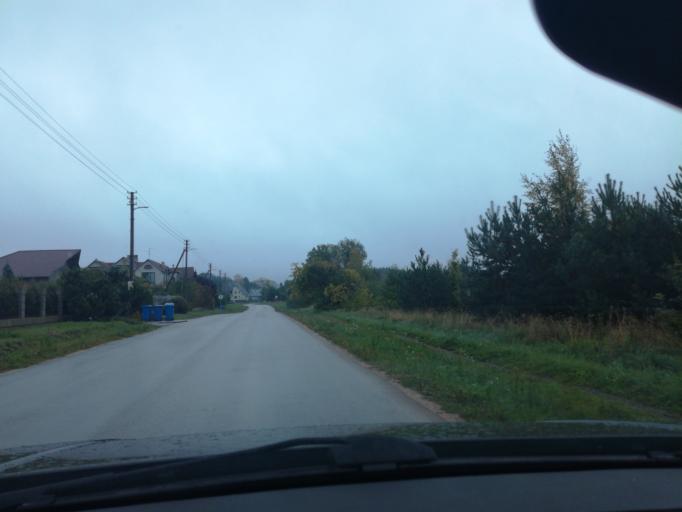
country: LT
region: Alytaus apskritis
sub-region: Alytus
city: Alytus
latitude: 54.3988
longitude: 24.0819
